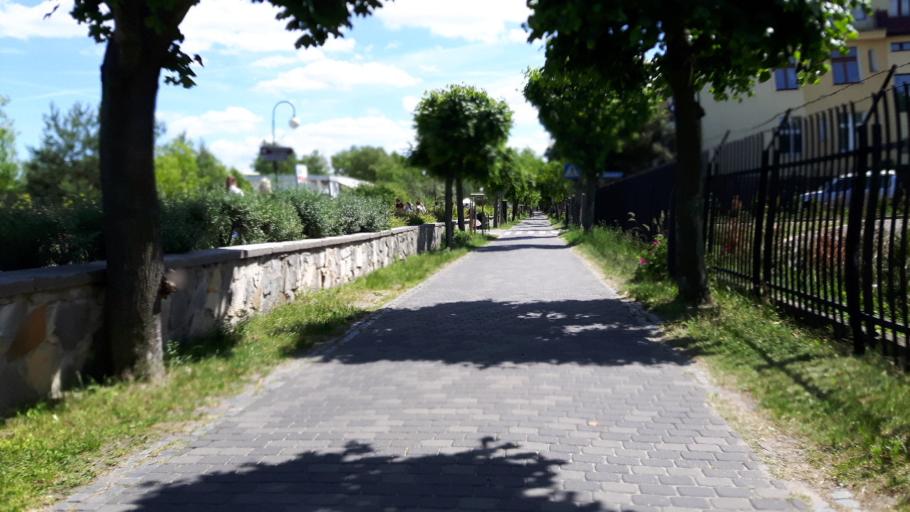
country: PL
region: Pomeranian Voivodeship
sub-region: Sopot
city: Sopot
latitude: 54.4410
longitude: 18.5755
